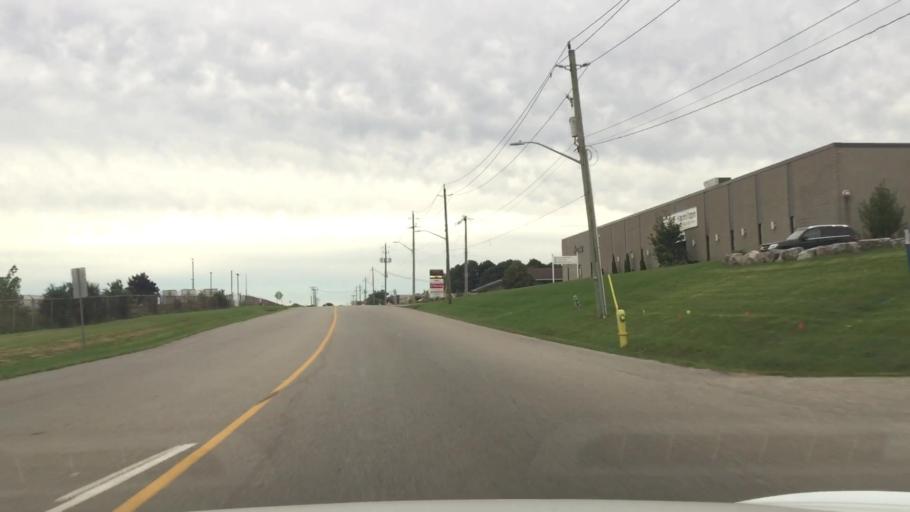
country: CA
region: Ontario
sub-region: Oxford County
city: Woodstock
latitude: 43.1215
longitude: -80.7246
